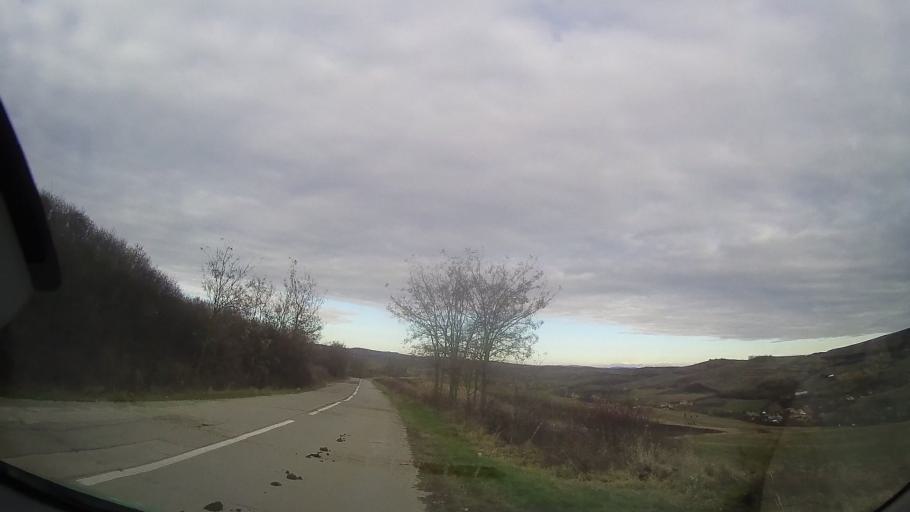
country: RO
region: Bistrita-Nasaud
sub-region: Comuna Micestii de Campie
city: Micestii de Campie
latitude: 46.8508
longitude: 24.3106
